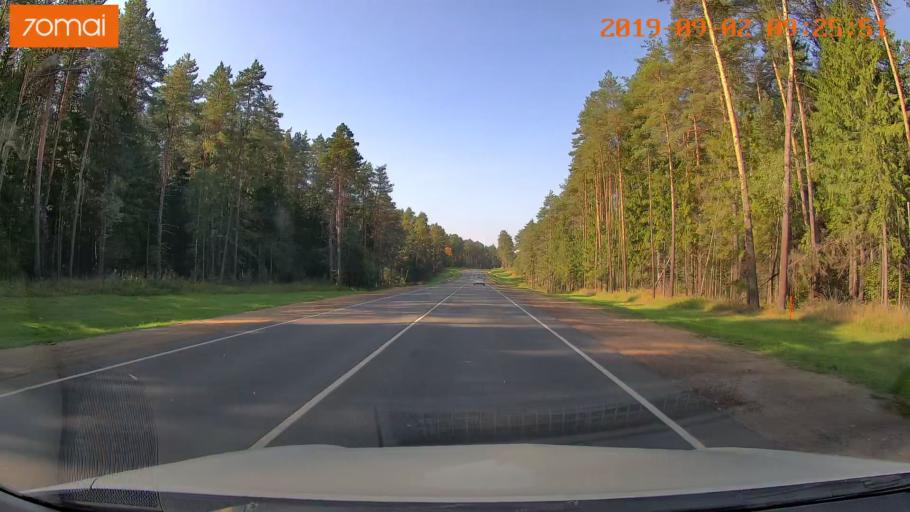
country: RU
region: Kaluga
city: Yukhnov
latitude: 54.7543
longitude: 35.2694
